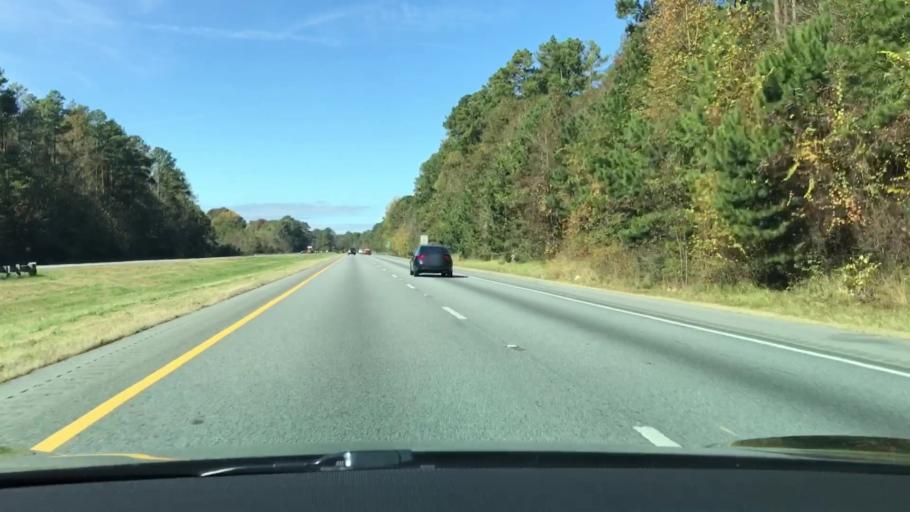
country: US
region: Georgia
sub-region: Morgan County
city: Madison
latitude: 33.5737
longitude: -83.5259
